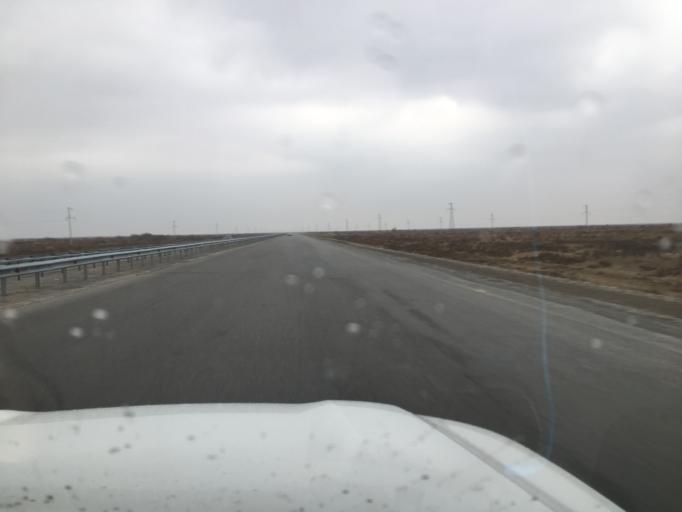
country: TM
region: Ahal
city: Kaka
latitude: 37.5017
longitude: 59.4537
